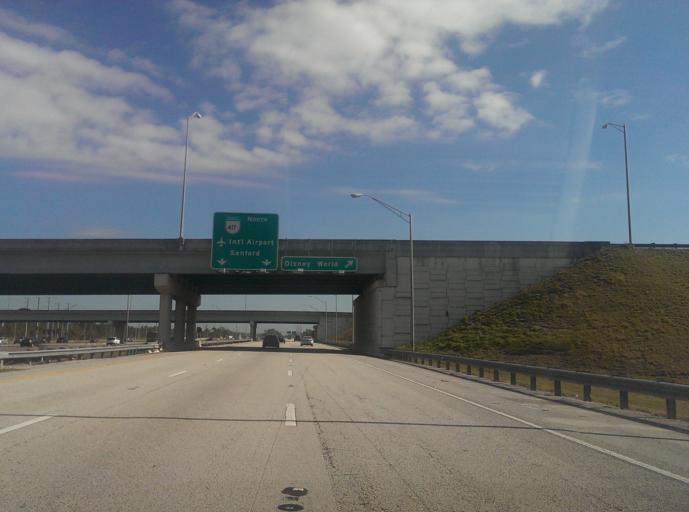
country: US
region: Florida
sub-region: Osceola County
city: Celebration
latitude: 28.3049
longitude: -81.5709
